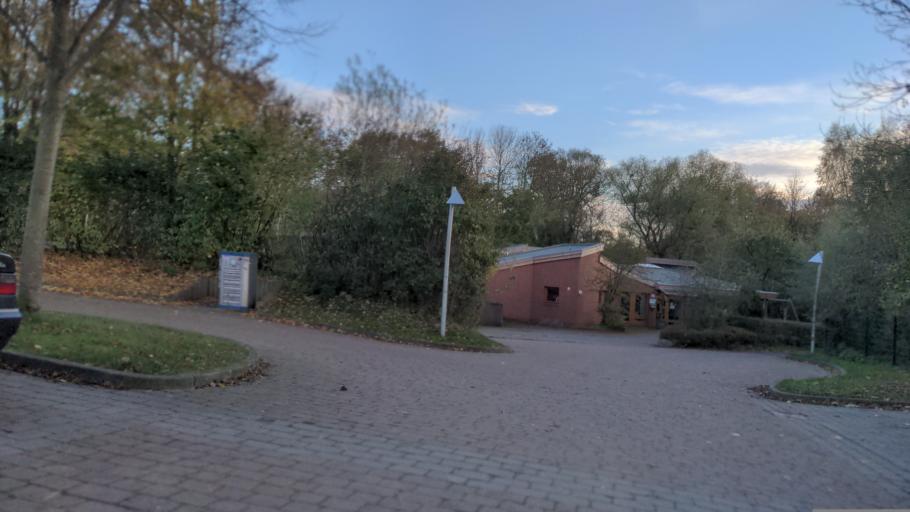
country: DE
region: Schleswig-Holstein
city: Reinfeld
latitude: 53.8299
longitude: 10.4834
